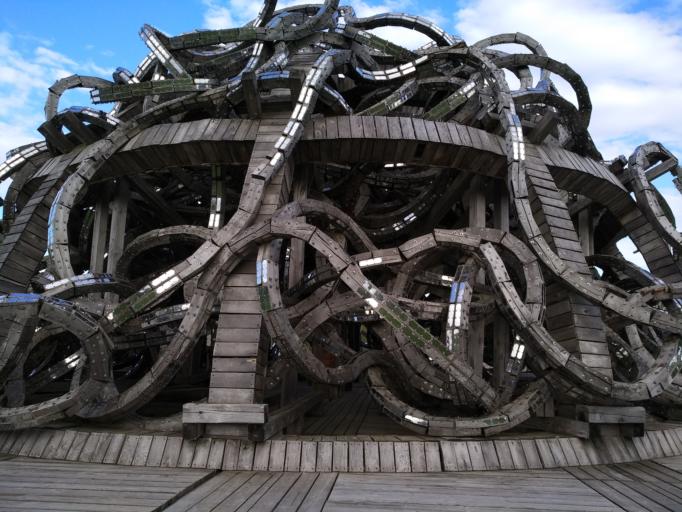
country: RU
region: Kaluga
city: Nikola-Lenivets
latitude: 54.7501
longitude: 35.6076
